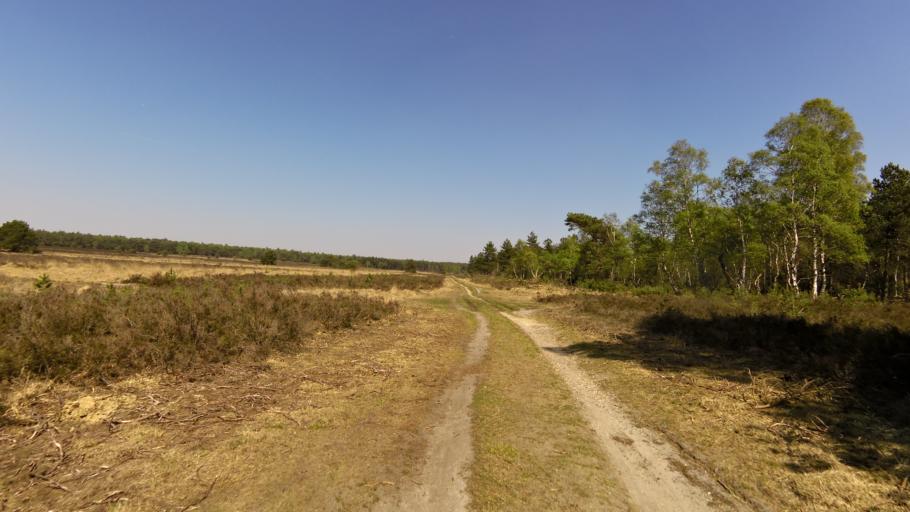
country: NL
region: Gelderland
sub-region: Gemeente Rozendaal
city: Rozendaal
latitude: 52.0328
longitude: 5.9486
